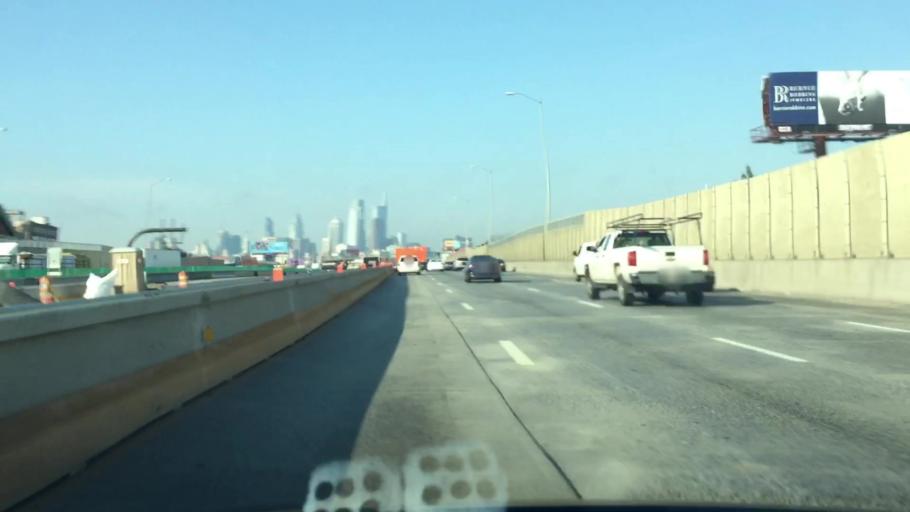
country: US
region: Pennsylvania
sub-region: Philadelphia County
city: Philadelphia
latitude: 39.9685
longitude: -75.1292
